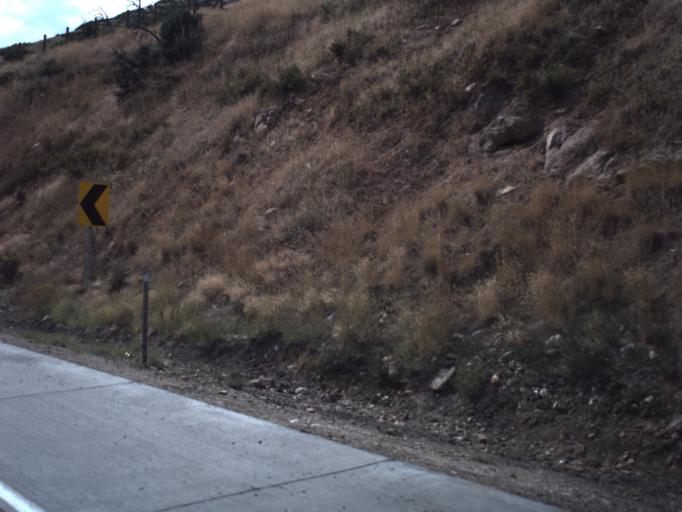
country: US
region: Utah
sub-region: Summit County
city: Snyderville
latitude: 40.7842
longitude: -111.4585
